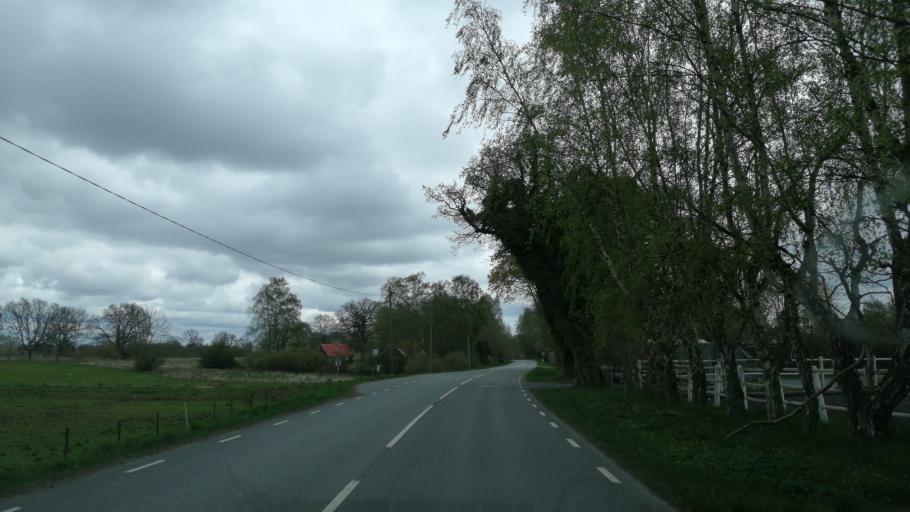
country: SE
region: Skane
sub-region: Kristianstads Kommun
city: Onnestad
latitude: 55.9945
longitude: 14.0449
